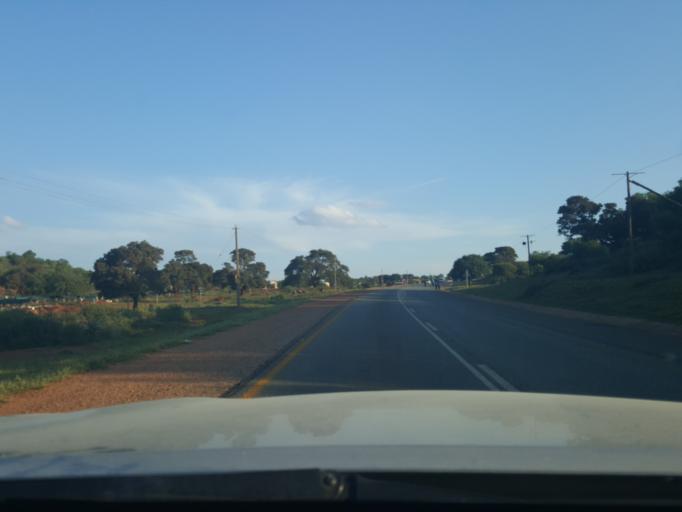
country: ZA
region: North-West
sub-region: Ngaka Modiri Molema District Municipality
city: Zeerust
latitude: -25.3202
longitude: 26.1230
